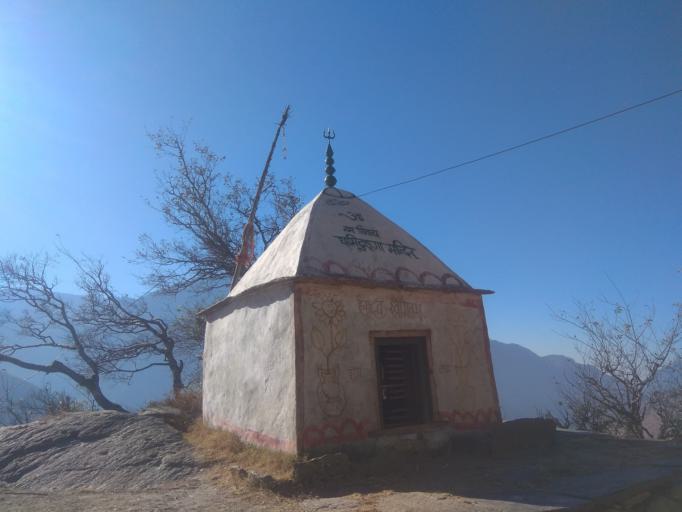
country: NP
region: Mid Western
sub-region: Bheri Zone
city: Dailekh
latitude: 29.2885
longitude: 81.7105
